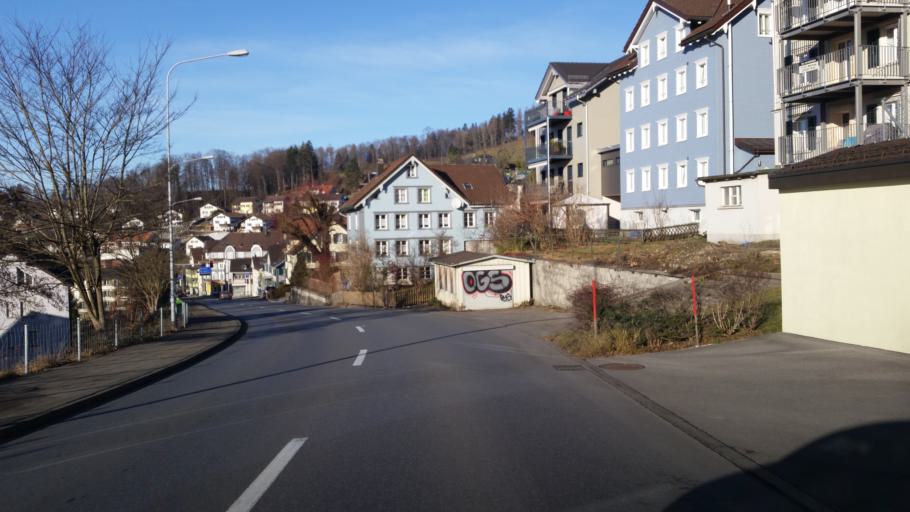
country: CH
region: Appenzell Ausserrhoden
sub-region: Bezirk Hinterland
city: Herisau
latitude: 47.3897
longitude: 9.2733
